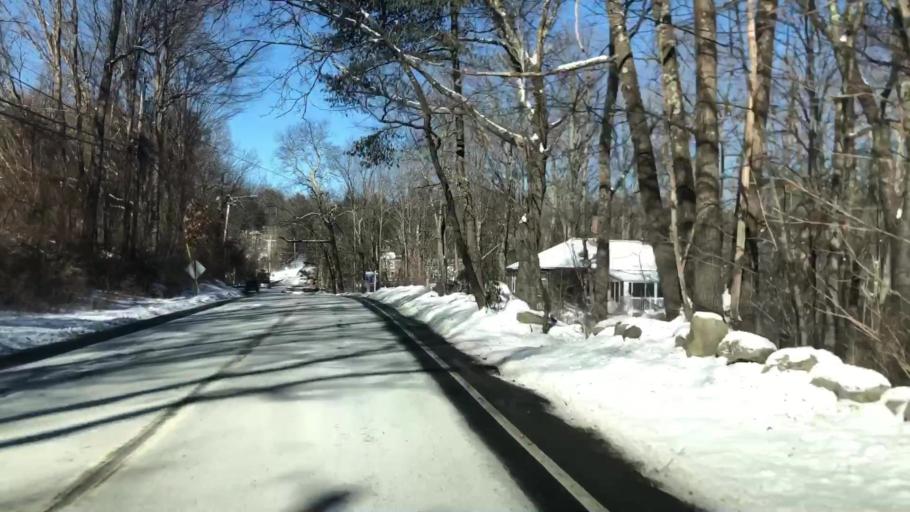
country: US
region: New Hampshire
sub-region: Hillsborough County
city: Bedford
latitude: 42.9409
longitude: -71.5271
